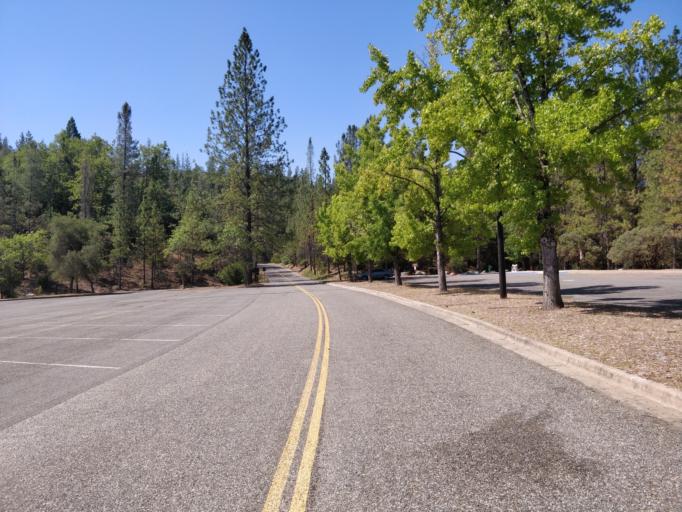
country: US
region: California
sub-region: Shasta County
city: Shasta
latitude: 40.6182
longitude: -122.5698
